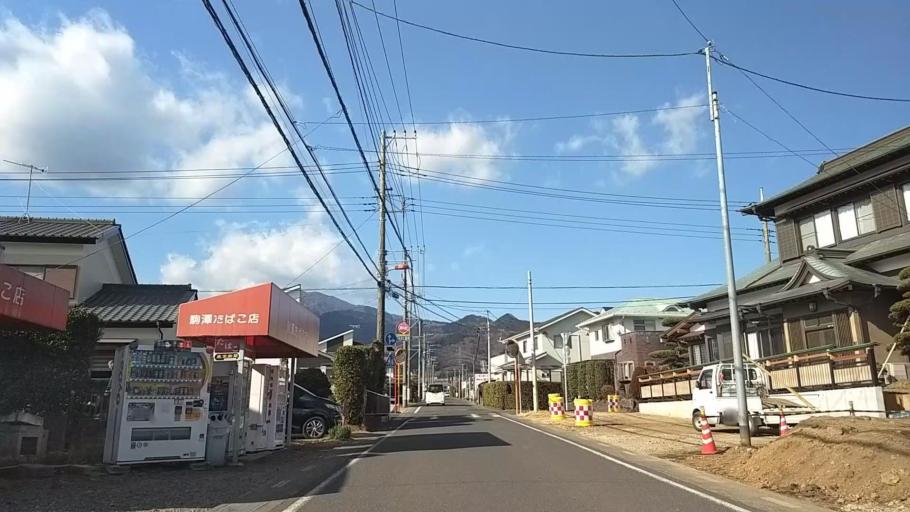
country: JP
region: Kanagawa
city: Isehara
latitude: 35.4089
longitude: 139.2913
